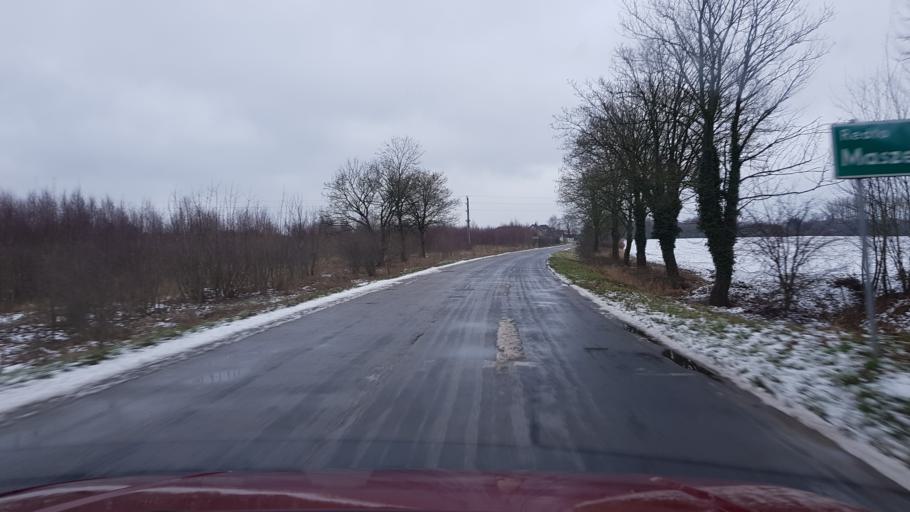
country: PL
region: West Pomeranian Voivodeship
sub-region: Powiat goleniowski
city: Nowogard
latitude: 53.6548
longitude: 15.1245
